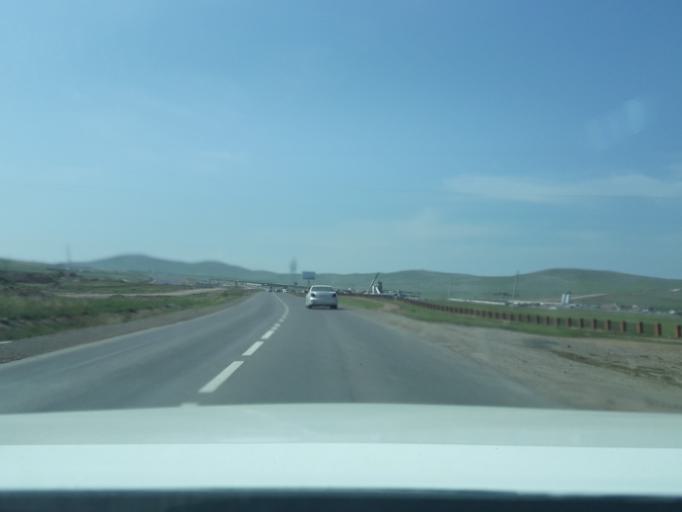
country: MN
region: Ulaanbaatar
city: Ulaanbaatar
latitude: 47.8239
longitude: 106.7649
